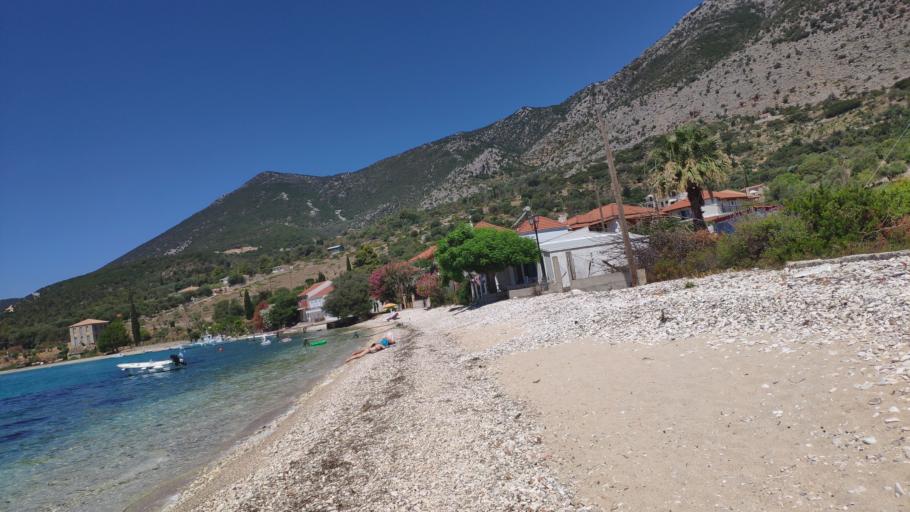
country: GR
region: West Greece
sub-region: Nomos Aitolias kai Akarnanias
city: Kandila
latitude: 38.6160
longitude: 20.9256
